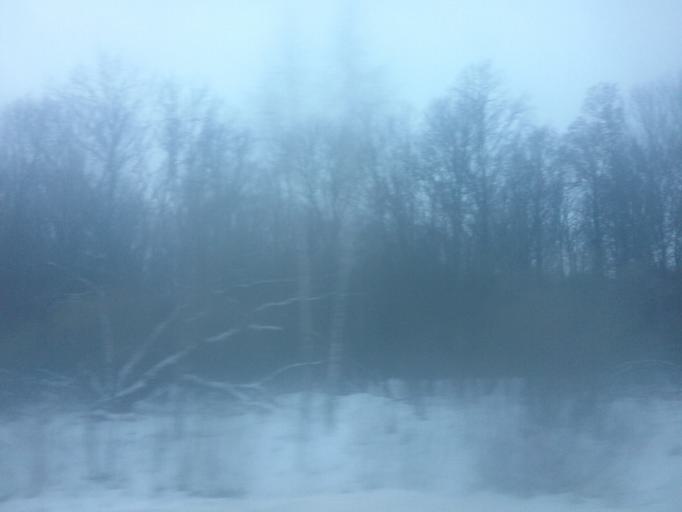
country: RU
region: Tula
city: Bogoroditsk
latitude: 53.8037
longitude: 38.1274
